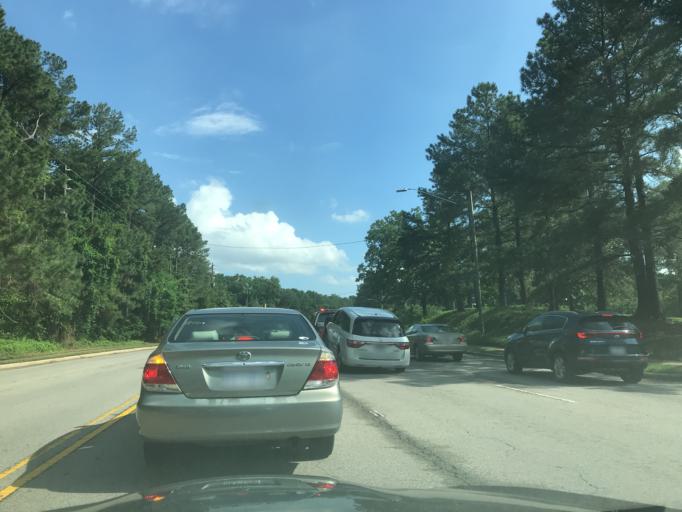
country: US
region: North Carolina
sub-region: Wake County
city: West Raleigh
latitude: 35.8663
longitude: -78.6379
